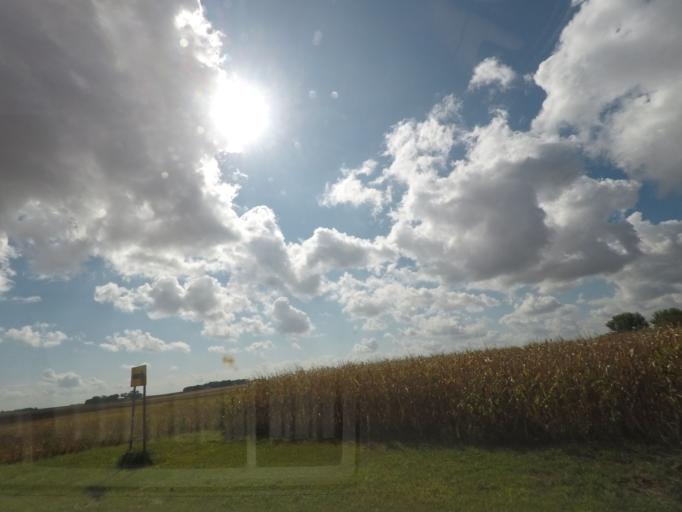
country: US
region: Iowa
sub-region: Story County
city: Nevada
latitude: 42.0007
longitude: -93.3193
